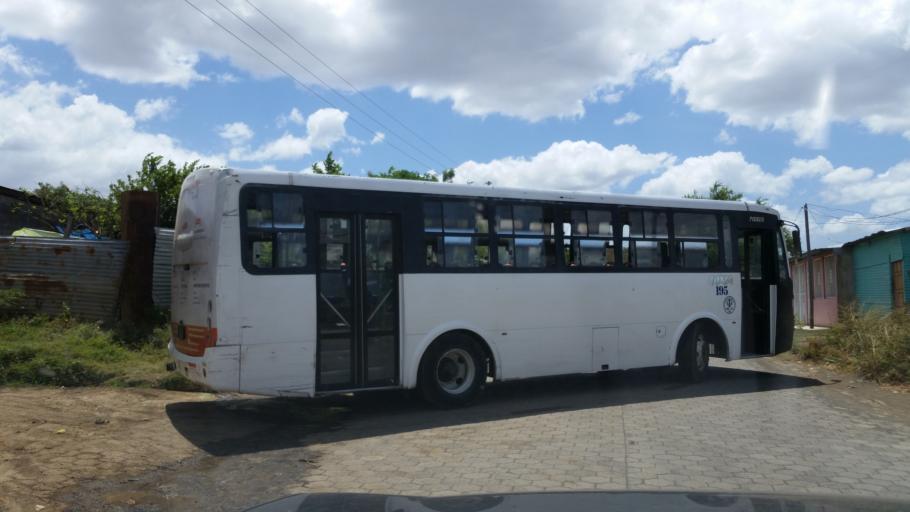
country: NI
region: Managua
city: Managua
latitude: 12.1110
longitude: -86.2089
